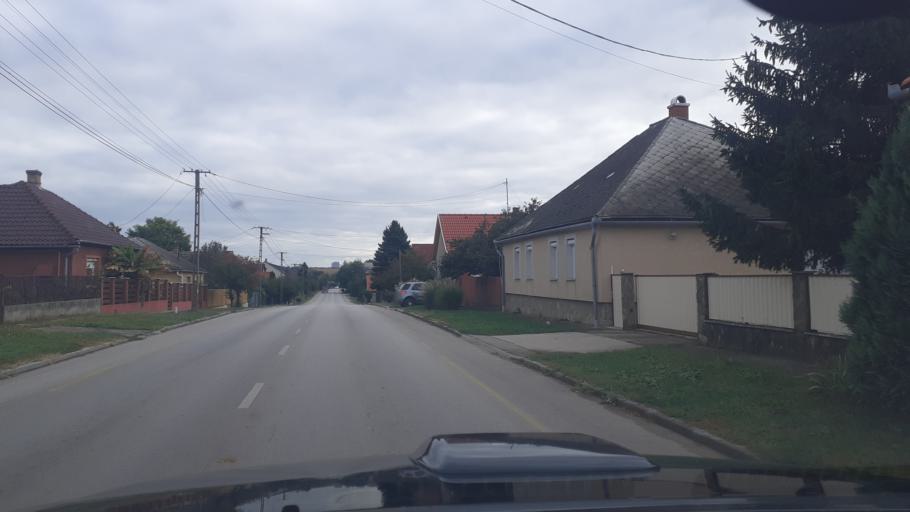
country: HU
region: Fejer
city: Baracs
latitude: 46.9142
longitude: 18.8725
